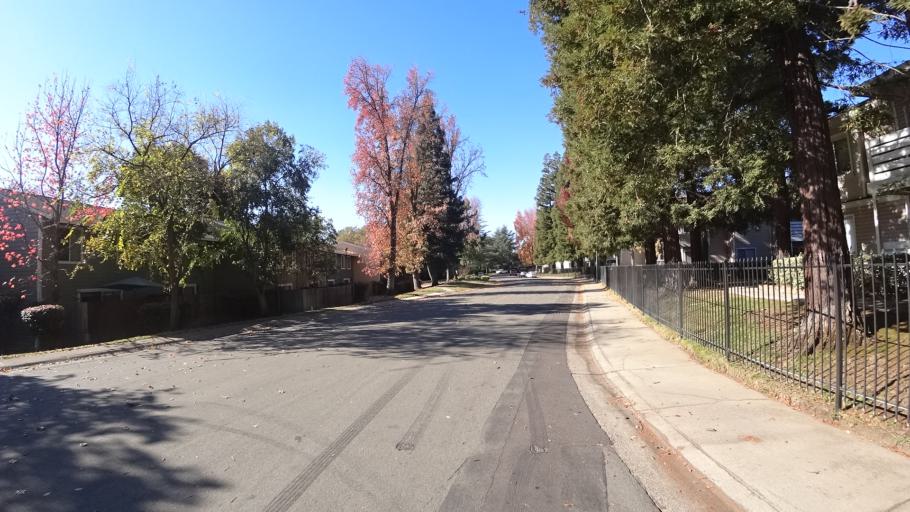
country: US
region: California
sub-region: Sacramento County
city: Foothill Farms
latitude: 38.6751
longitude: -121.3212
